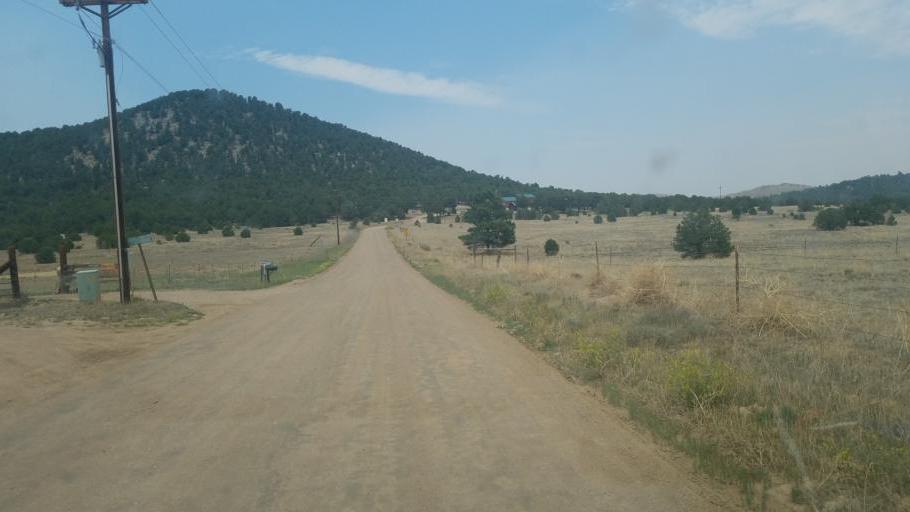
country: US
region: Colorado
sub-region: Custer County
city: Westcliffe
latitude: 38.2954
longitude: -105.4912
